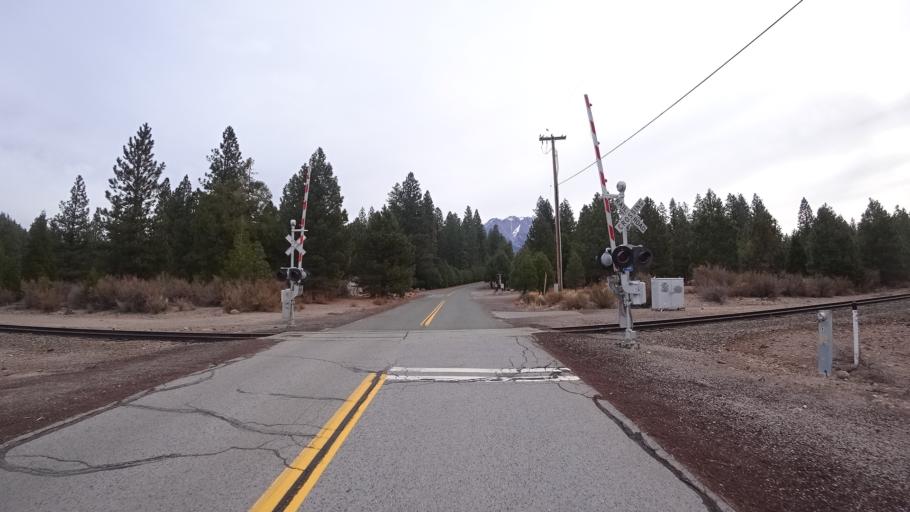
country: US
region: California
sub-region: Siskiyou County
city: Weed
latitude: 41.4095
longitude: -122.3781
